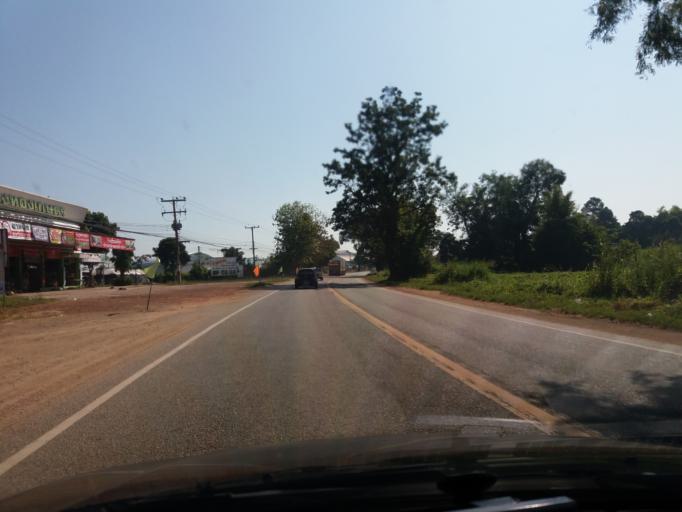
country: TH
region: Kamphaeng Phet
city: Khlong Khlung
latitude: 16.1777
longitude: 99.7865
